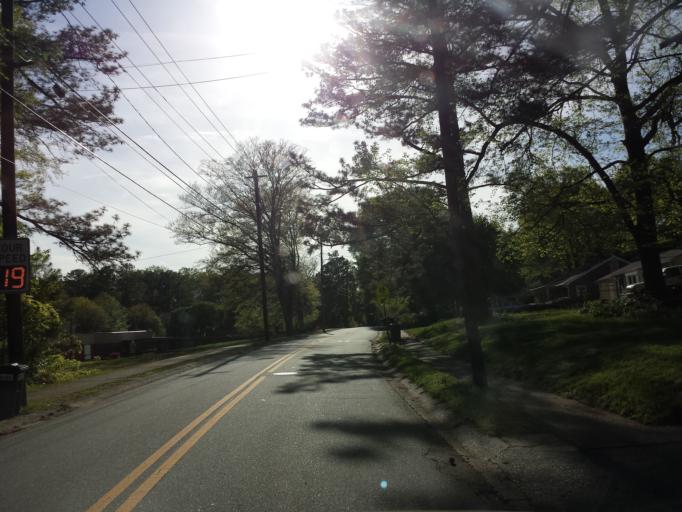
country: US
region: Georgia
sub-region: Cobb County
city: Marietta
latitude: 33.9575
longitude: -84.5610
